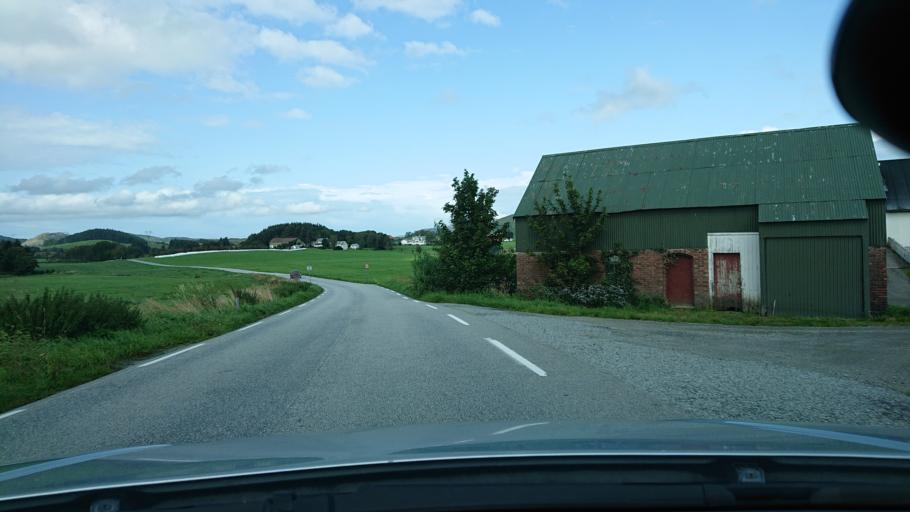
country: NO
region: Rogaland
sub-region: Gjesdal
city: Algard
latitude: 58.6966
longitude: 5.7812
